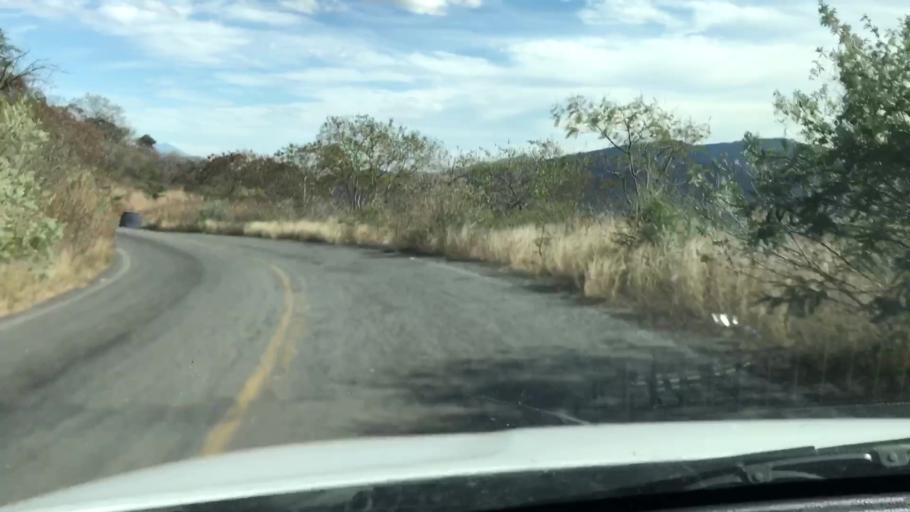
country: MX
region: Jalisco
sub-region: Zacoalco de Torres
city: Barranca de Otates (Barranca de Otatan)
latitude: 20.2455
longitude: -103.6717
